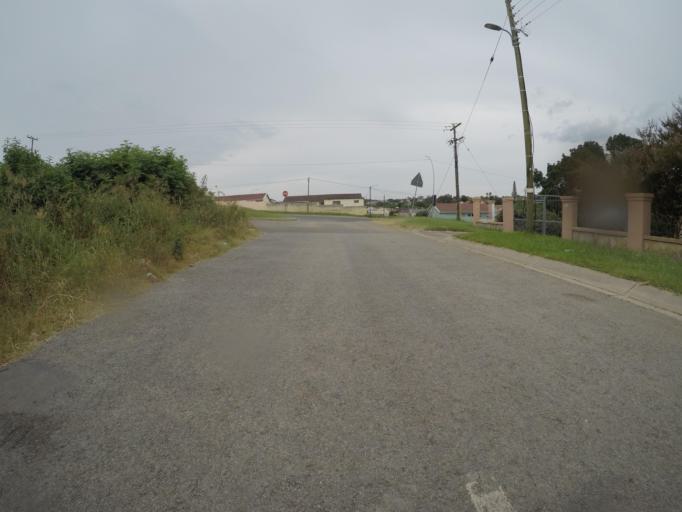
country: ZA
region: Eastern Cape
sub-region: Buffalo City Metropolitan Municipality
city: East London
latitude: -32.9972
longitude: 27.8484
